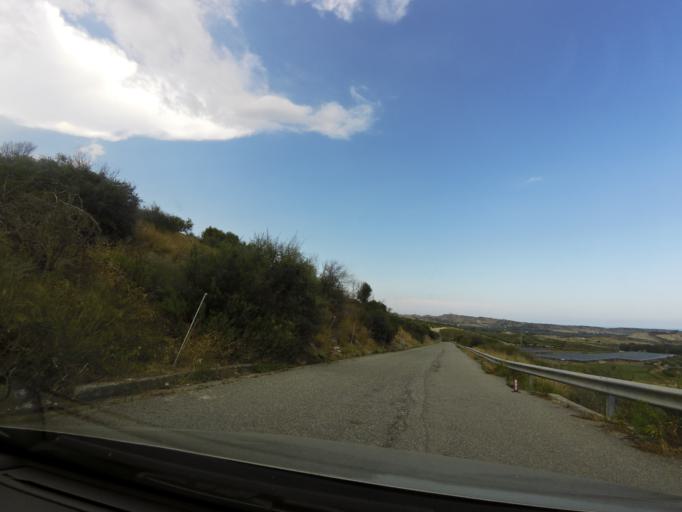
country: IT
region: Calabria
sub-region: Provincia di Reggio Calabria
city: Camini
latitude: 38.4254
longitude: 16.5134
